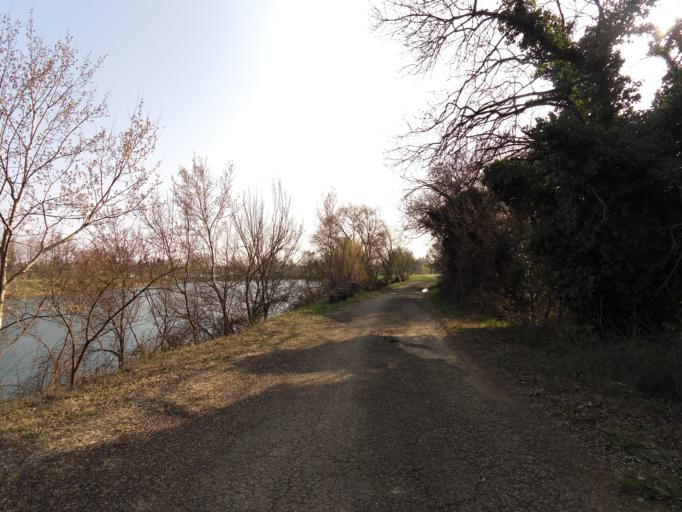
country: FR
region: Languedoc-Roussillon
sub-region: Departement du Gard
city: Vestric-et-Candiac
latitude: 43.7282
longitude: 4.2641
